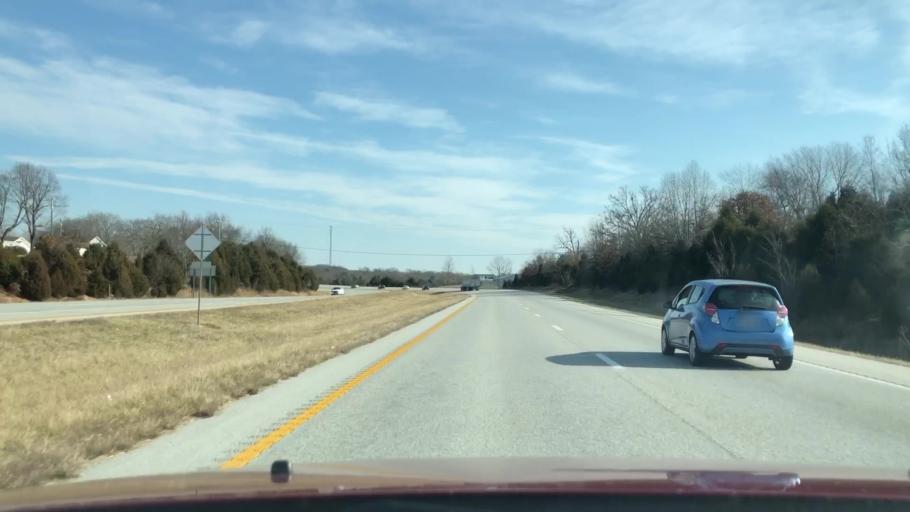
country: US
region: Missouri
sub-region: Webster County
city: Rogersville
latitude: 37.1520
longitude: -92.9417
